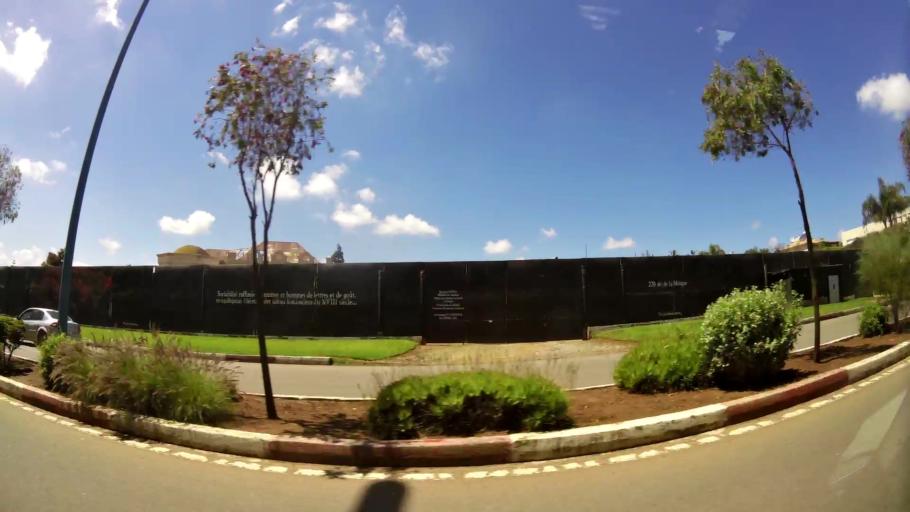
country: MA
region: Grand Casablanca
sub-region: Casablanca
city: Casablanca
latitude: 33.5298
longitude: -7.6303
